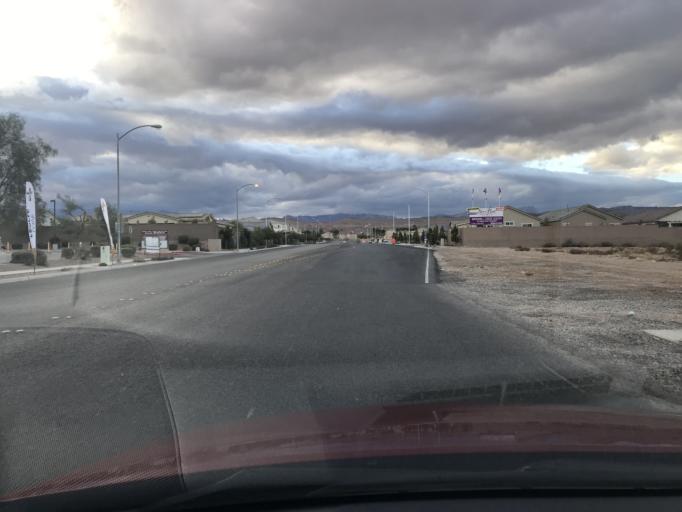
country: US
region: Nevada
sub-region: Clark County
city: Enterprise
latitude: 36.0405
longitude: -115.2749
